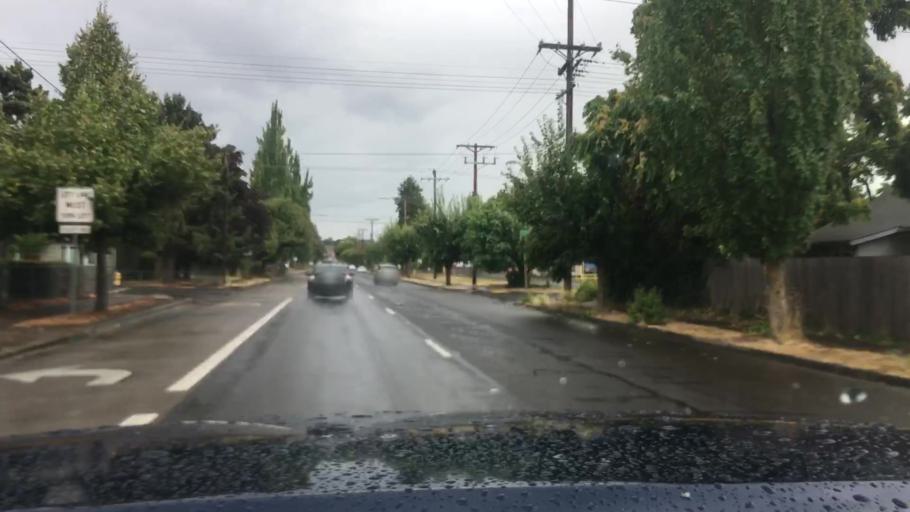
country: US
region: Oregon
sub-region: Lane County
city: Springfield
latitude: 44.0509
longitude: -123.0233
